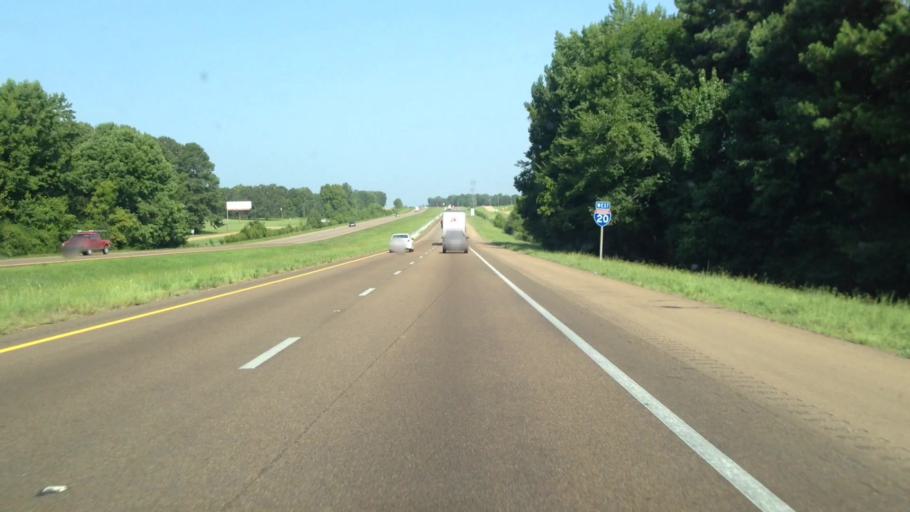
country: US
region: Mississippi
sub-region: Hinds County
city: Clinton
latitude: 32.3433
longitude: -90.3563
